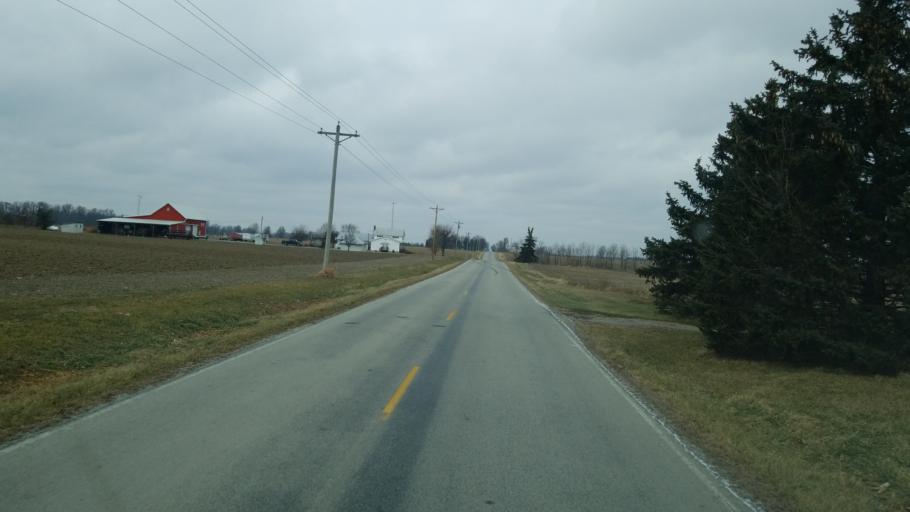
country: US
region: Ohio
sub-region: Hardin County
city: Forest
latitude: 40.7834
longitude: -83.4195
